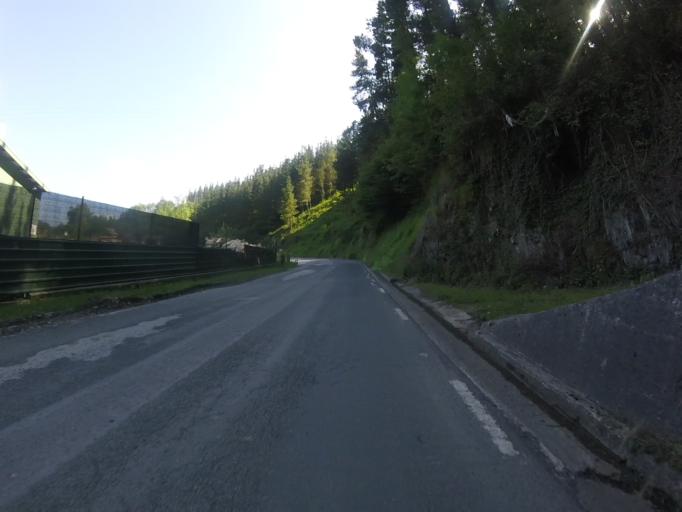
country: ES
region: Basque Country
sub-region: Provincia de Guipuzcoa
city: Ormaiztegui
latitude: 43.0623
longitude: -2.2379
